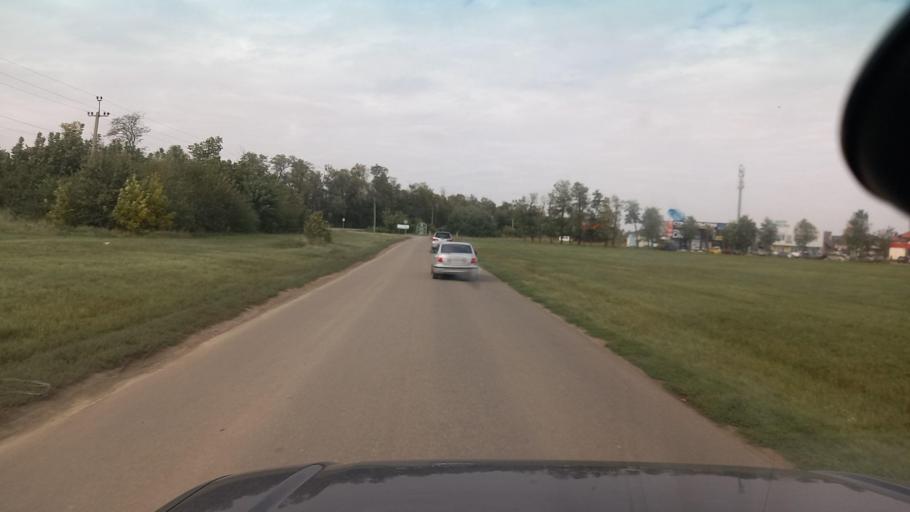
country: RU
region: Krasnodarskiy
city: Krasnodar
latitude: 45.1152
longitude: 38.9202
